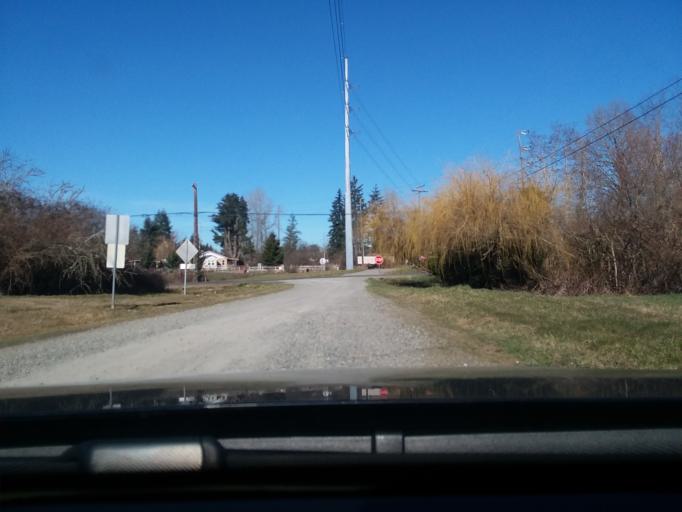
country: US
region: Washington
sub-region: Pierce County
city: Waller
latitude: 47.1837
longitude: -122.3778
